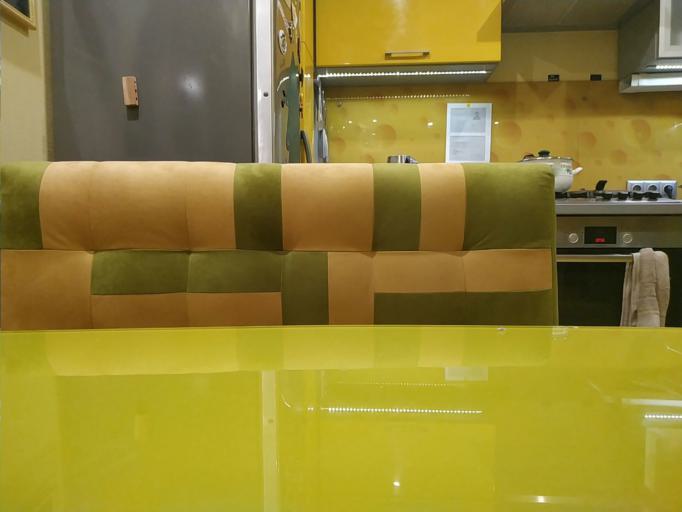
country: RU
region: Murmansk
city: Alakurtti
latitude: 66.1806
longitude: 30.2991
